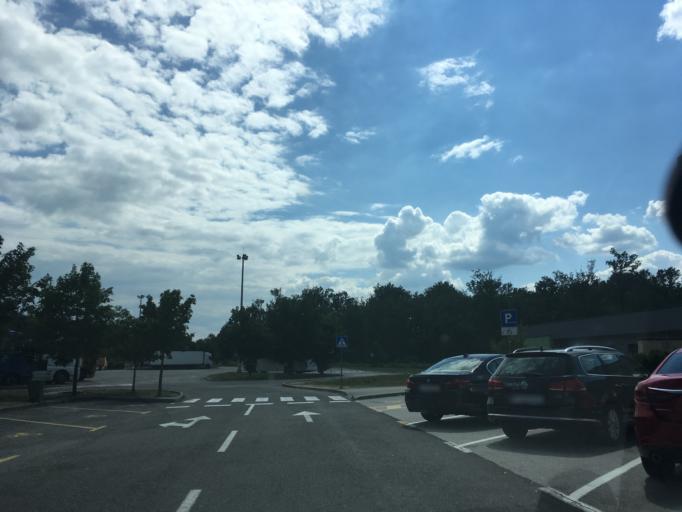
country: HR
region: Karlovacka
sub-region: Grad Karlovac
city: Karlovac
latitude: 45.5597
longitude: 15.6071
